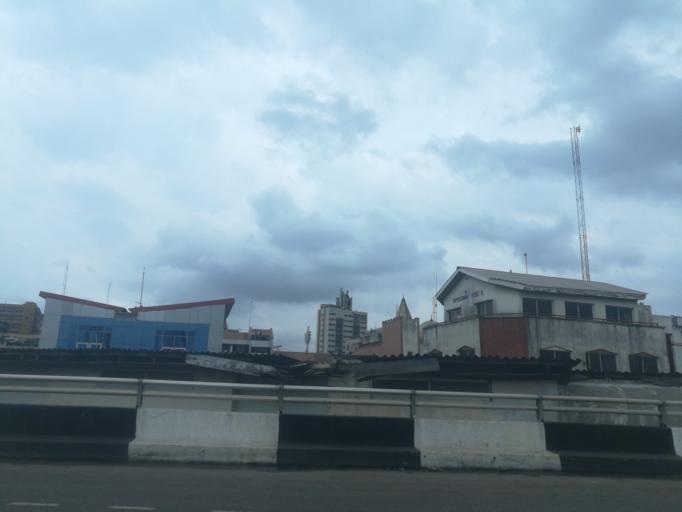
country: NG
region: Lagos
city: Lagos
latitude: 6.4471
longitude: 3.4074
